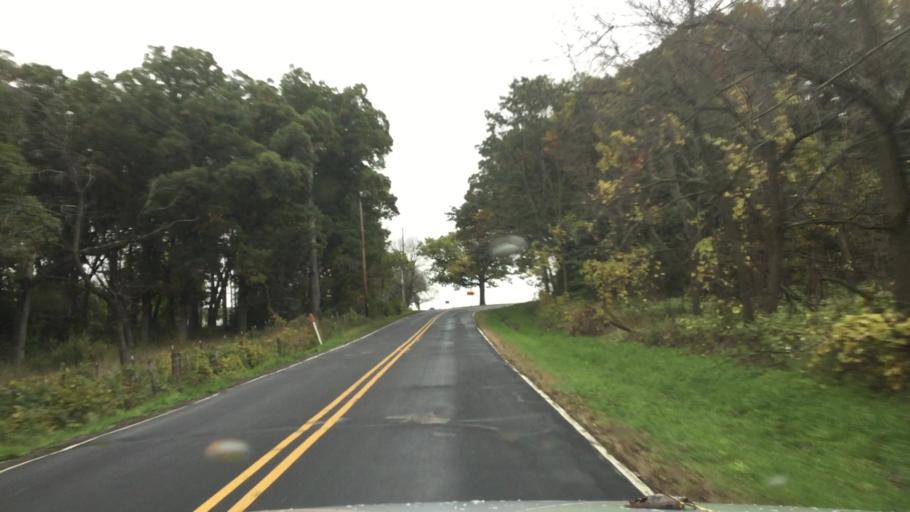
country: US
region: Wisconsin
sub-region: Racine County
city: Waterford
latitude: 42.7602
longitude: -88.1623
